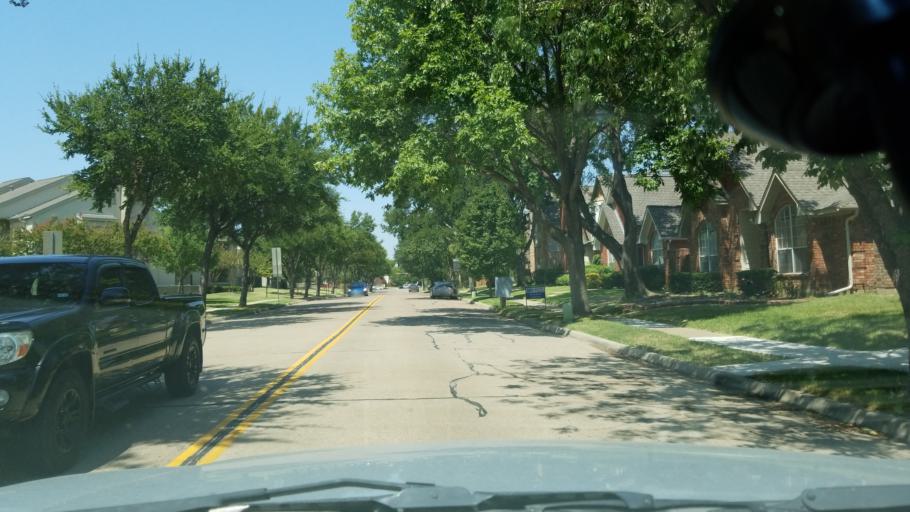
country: US
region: Texas
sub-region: Dallas County
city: Farmers Branch
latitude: 32.9301
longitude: -96.9494
